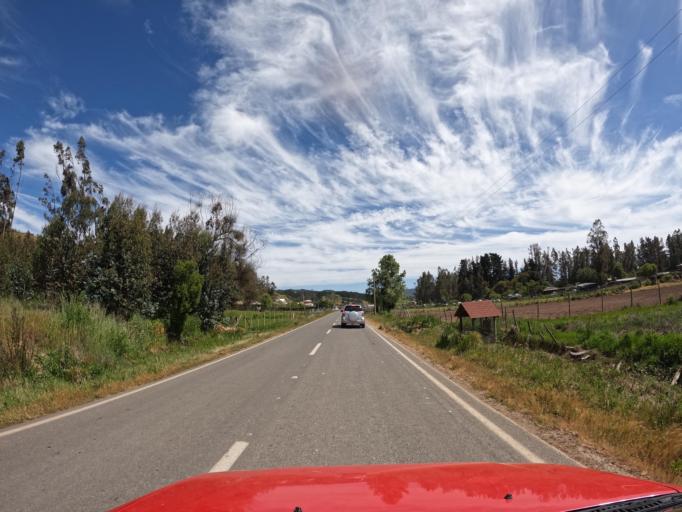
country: CL
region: Maule
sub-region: Provincia de Talca
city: Constitucion
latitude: -35.0149
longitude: -72.0377
